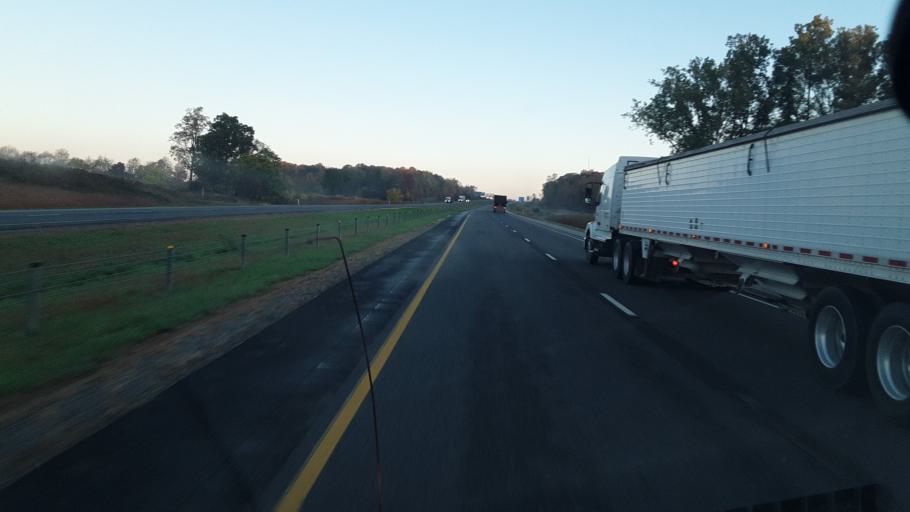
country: US
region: Indiana
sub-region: DeKalb County
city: Waterloo
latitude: 41.5000
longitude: -85.0545
